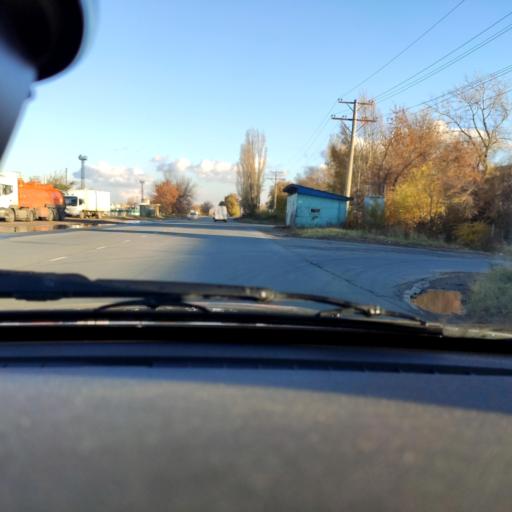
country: RU
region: Samara
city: Tol'yatti
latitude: 53.5328
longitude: 49.4524
